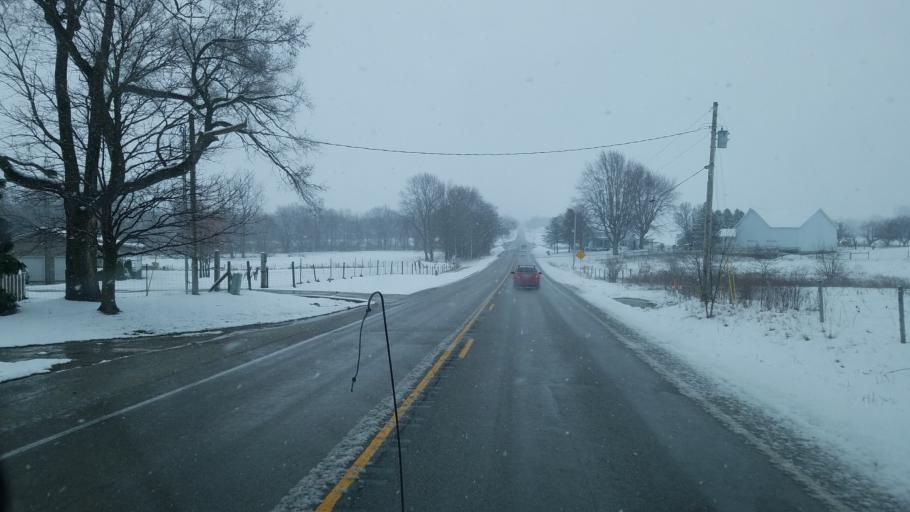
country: US
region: Indiana
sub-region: Randolph County
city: Parker City
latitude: 40.0618
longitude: -85.2508
